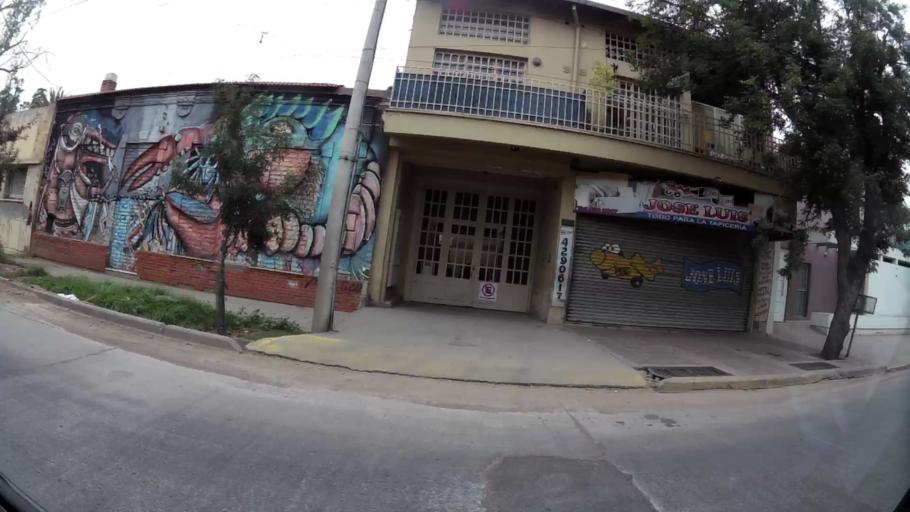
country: AR
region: Mendoza
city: Mendoza
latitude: -32.8878
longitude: -68.8306
